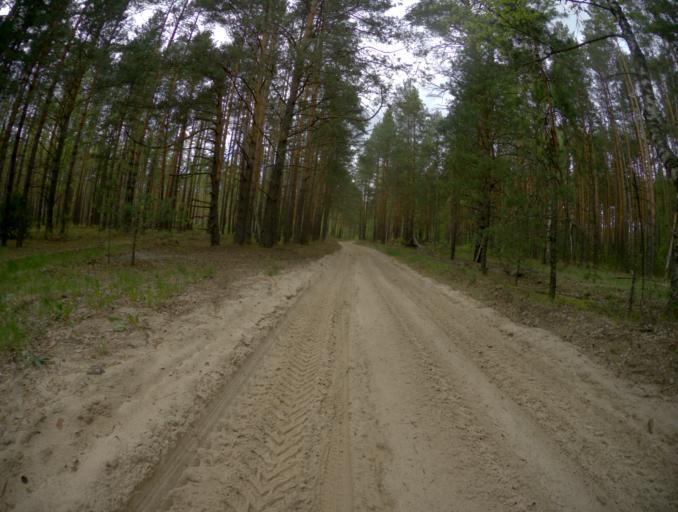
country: RU
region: Rjazan
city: Gus'-Zheleznyy
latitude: 55.0219
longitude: 41.1818
